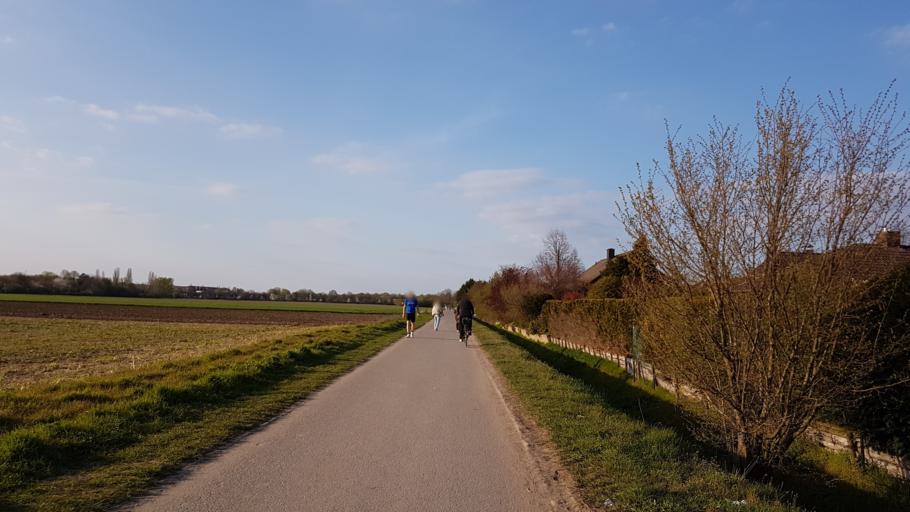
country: DE
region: Lower Saxony
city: Ronnenberg
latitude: 52.3334
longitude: 9.6829
